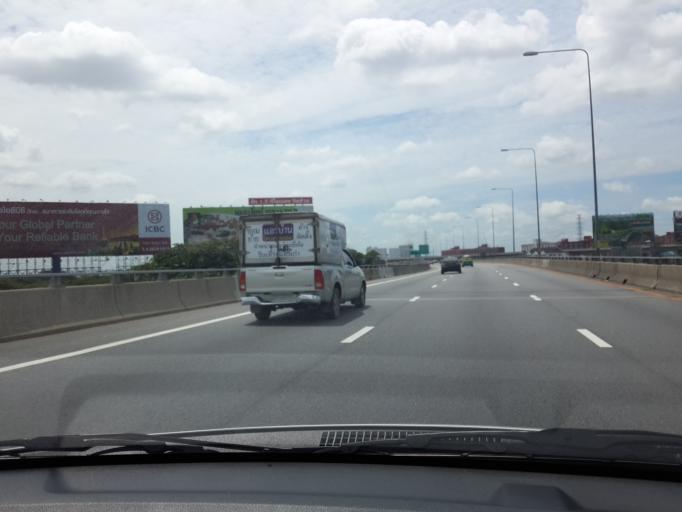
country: TH
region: Bangkok
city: Watthana
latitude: 13.7451
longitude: 100.6097
